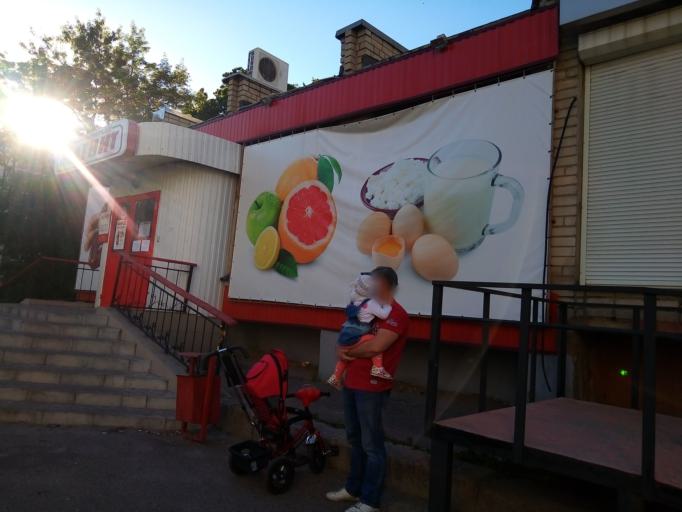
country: RU
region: Kursk
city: Kursk
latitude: 51.7464
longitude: 36.1852
